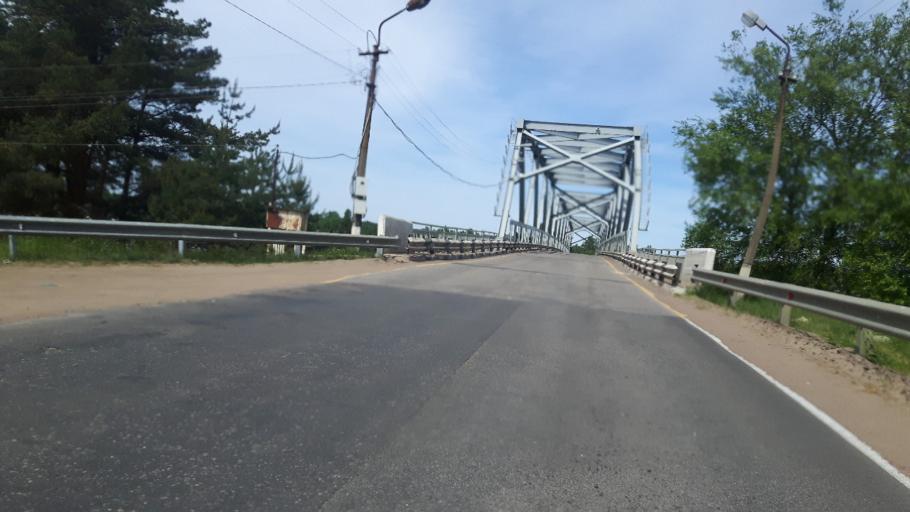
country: RU
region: Leningrad
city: Ust'-Luga
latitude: 59.6519
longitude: 28.2591
